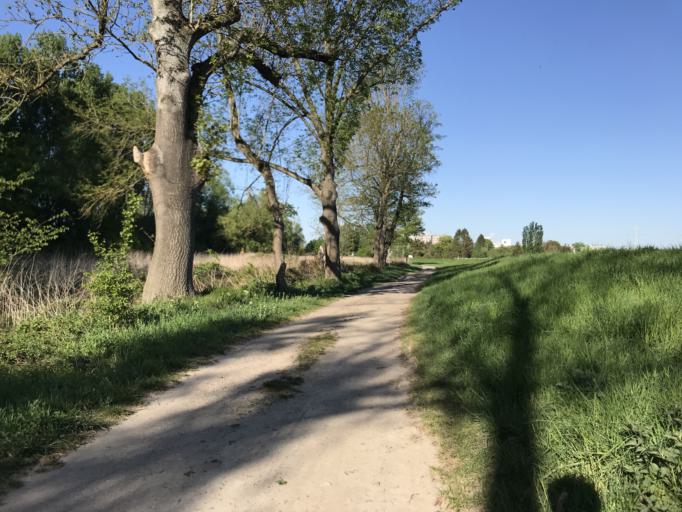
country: DE
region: Rheinland-Pfalz
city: Budenheim
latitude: 50.0274
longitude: 8.1613
